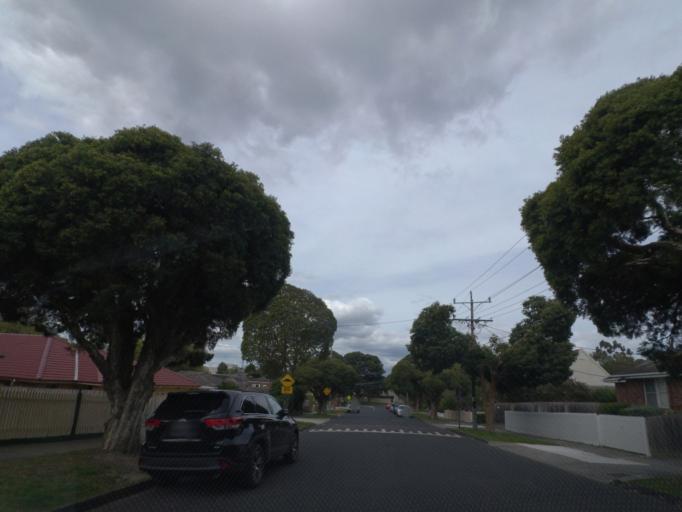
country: AU
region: Victoria
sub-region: Whitehorse
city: Box Hill
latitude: -37.8216
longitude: 145.1175
